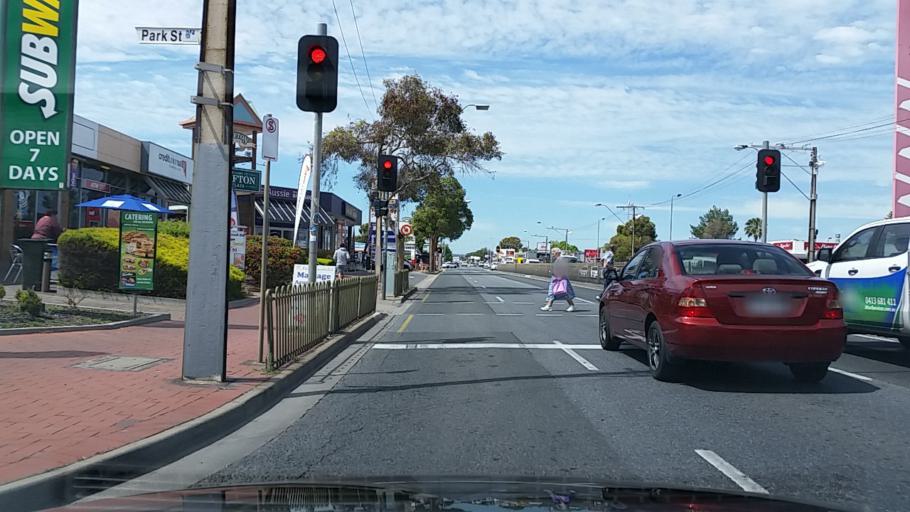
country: AU
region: South Australia
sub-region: Prospect
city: Prospect
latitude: -34.8756
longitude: 138.6022
